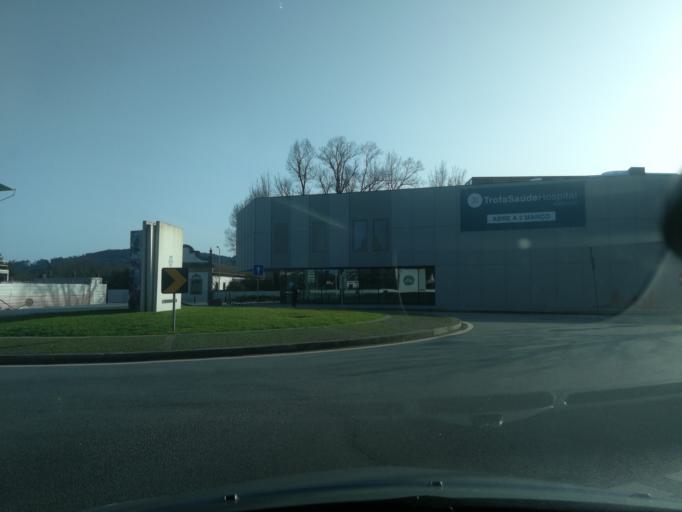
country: PT
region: Braga
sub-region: Barcelos
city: Barcelos
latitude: 41.5323
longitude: -8.6136
